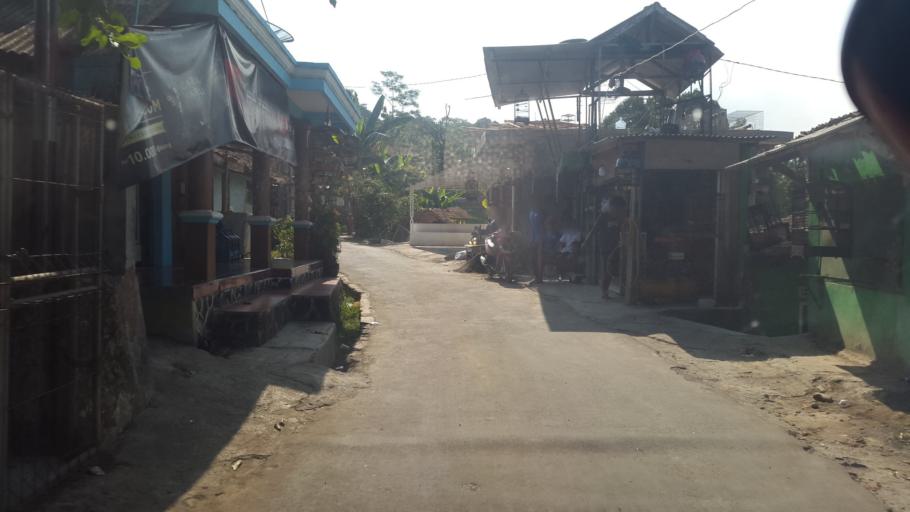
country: ID
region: West Java
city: Cicurug
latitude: -6.8348
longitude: 106.7357
